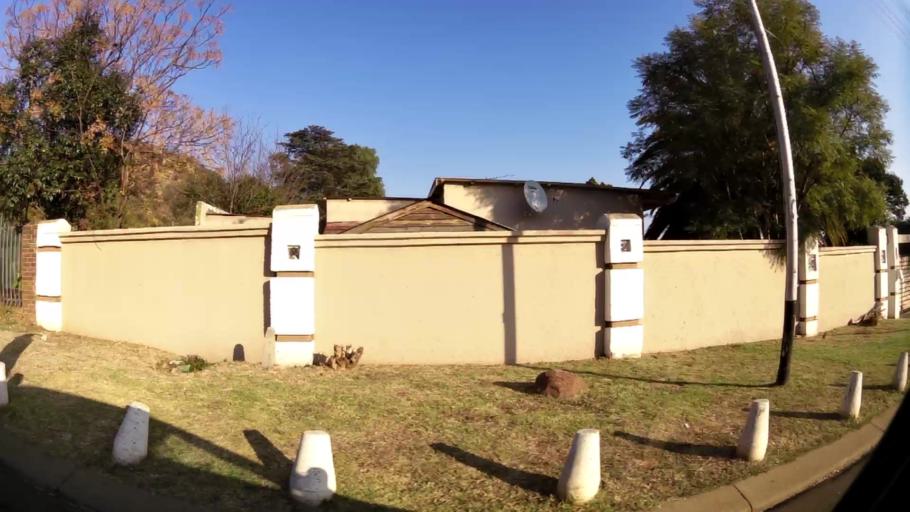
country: ZA
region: Gauteng
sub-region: City of Johannesburg Metropolitan Municipality
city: Soweto
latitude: -26.2768
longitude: 27.9607
